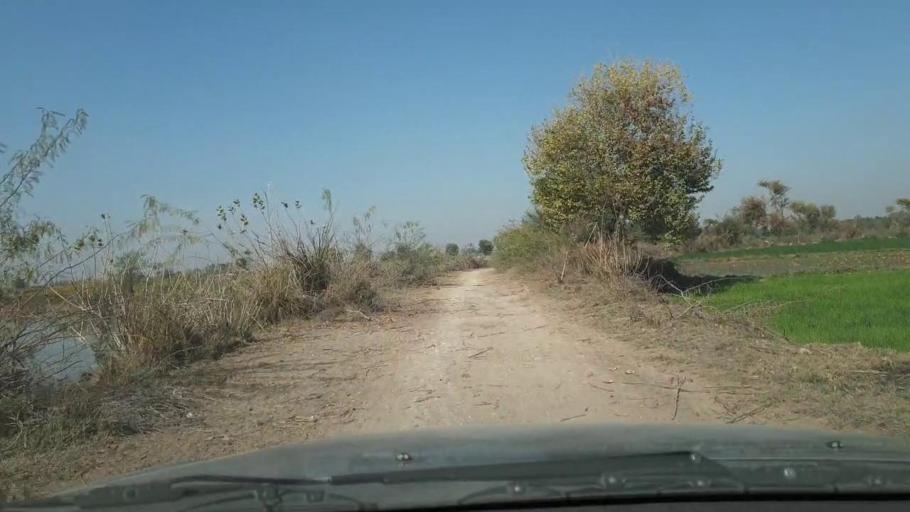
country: PK
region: Sindh
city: Adilpur
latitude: 27.8903
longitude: 69.2557
